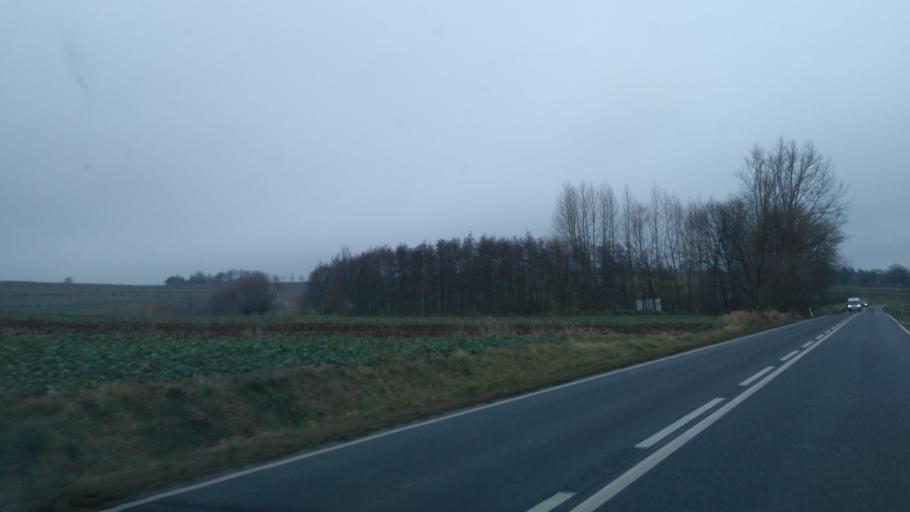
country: PL
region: Subcarpathian Voivodeship
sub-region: Powiat jaroslawski
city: Pruchnik
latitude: 49.9103
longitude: 22.5569
